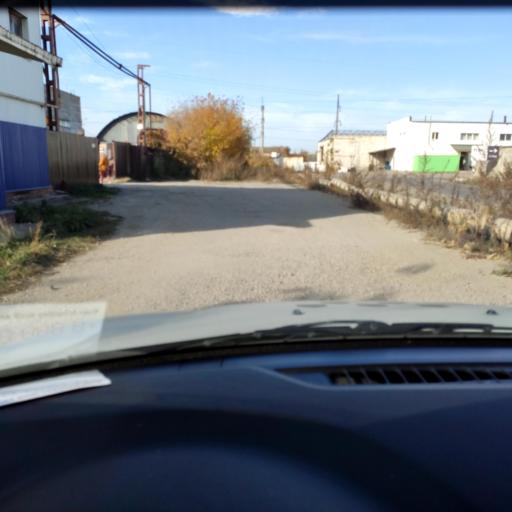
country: RU
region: Samara
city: Tol'yatti
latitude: 53.5242
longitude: 49.4702
